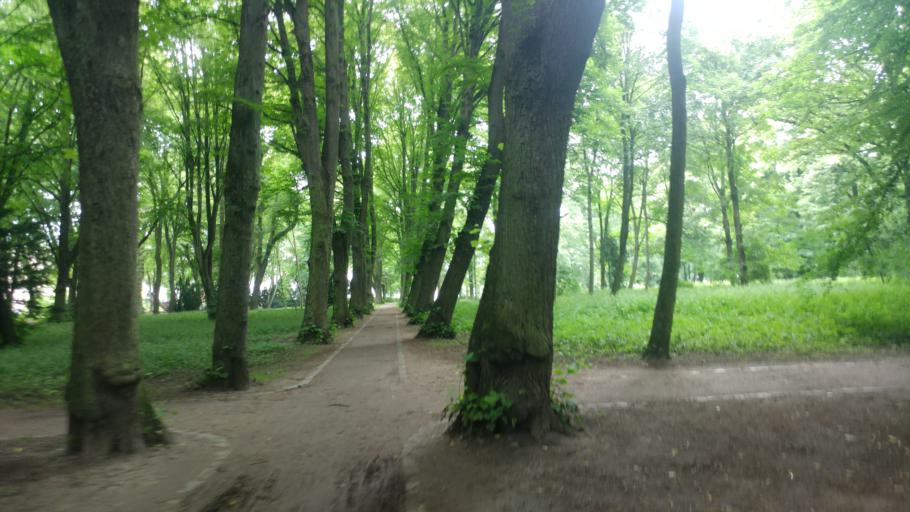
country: DE
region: Mecklenburg-Vorpommern
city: Rostock
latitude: 54.0830
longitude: 12.1168
